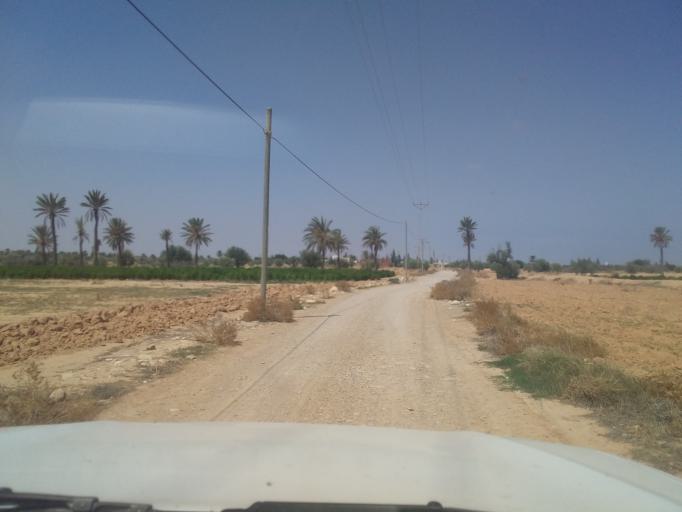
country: TN
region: Qabis
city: Matmata
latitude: 33.5957
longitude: 10.2829
